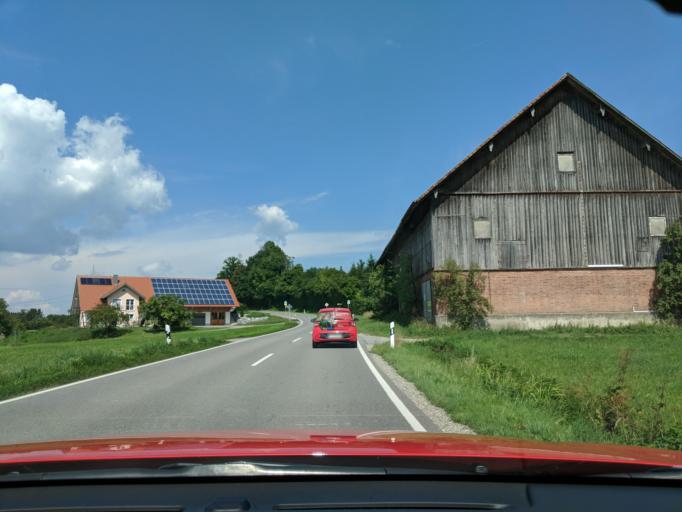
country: DE
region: Baden-Wuerttemberg
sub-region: Tuebingen Region
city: Wangen im Allgau
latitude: 47.7181
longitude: 9.8216
